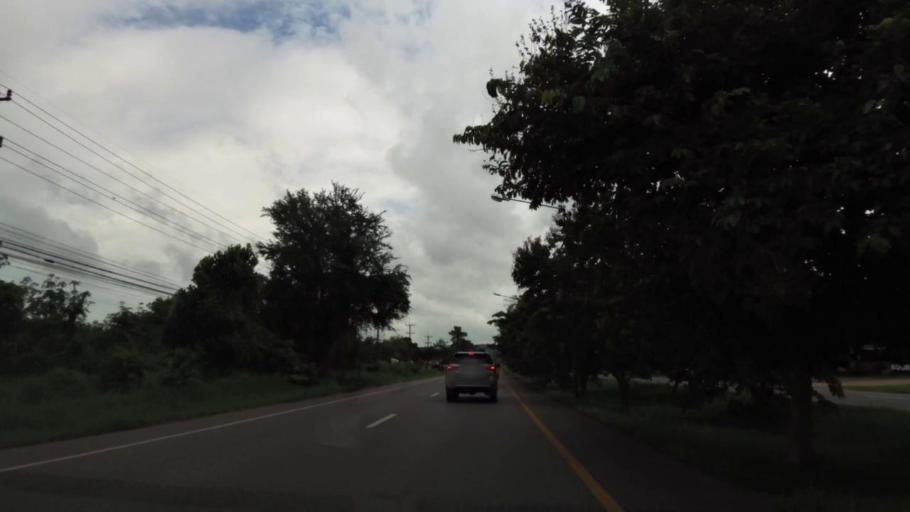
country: TH
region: Chanthaburi
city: Na Yai Am
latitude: 12.7322
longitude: 101.9081
